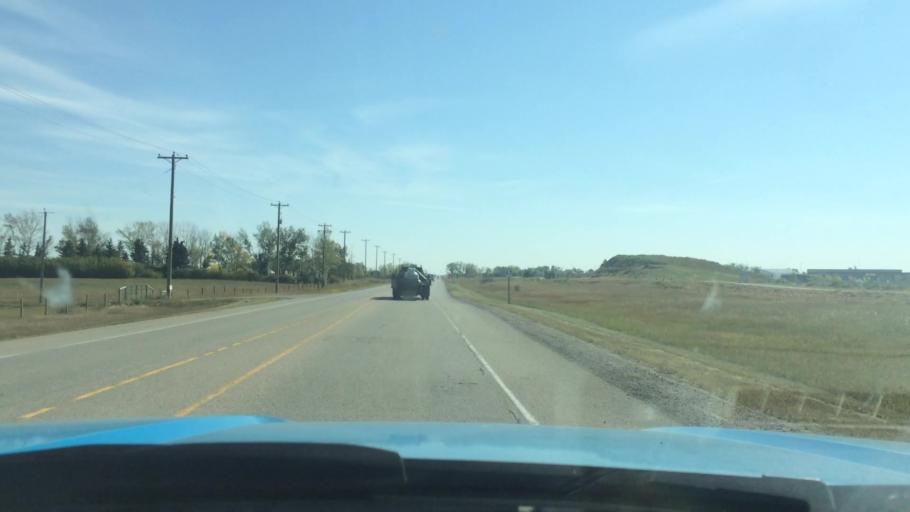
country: CA
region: Alberta
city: Airdrie
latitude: 51.2124
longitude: -113.9771
